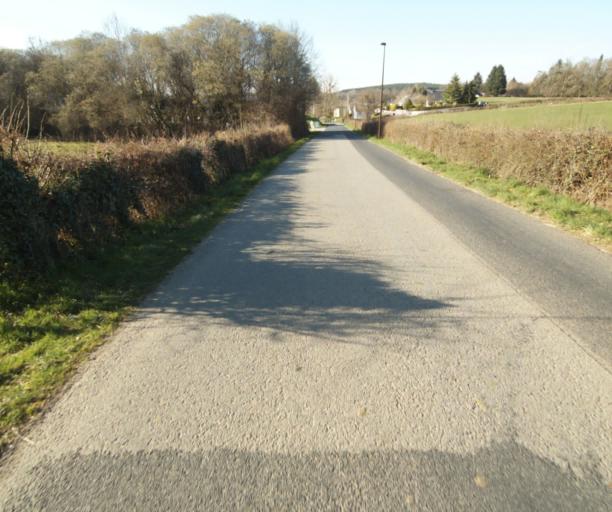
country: FR
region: Limousin
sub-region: Departement de la Correze
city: Chamboulive
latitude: 45.4666
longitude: 1.7270
